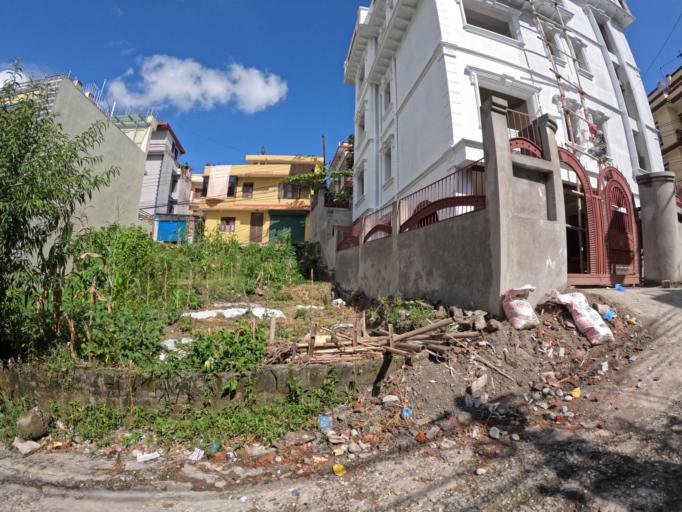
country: NP
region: Central Region
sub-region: Bagmati Zone
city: Kathmandu
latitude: 27.7492
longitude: 85.3330
